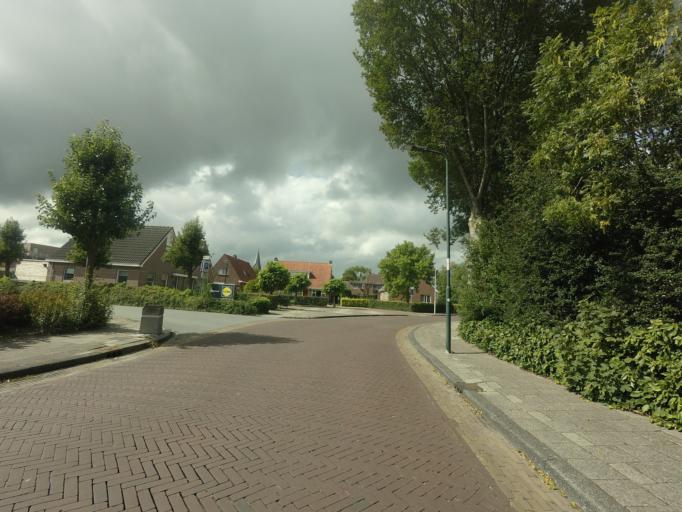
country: NL
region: Friesland
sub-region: Gemeente Skarsterlan
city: Joure
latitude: 52.9660
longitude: 5.8012
